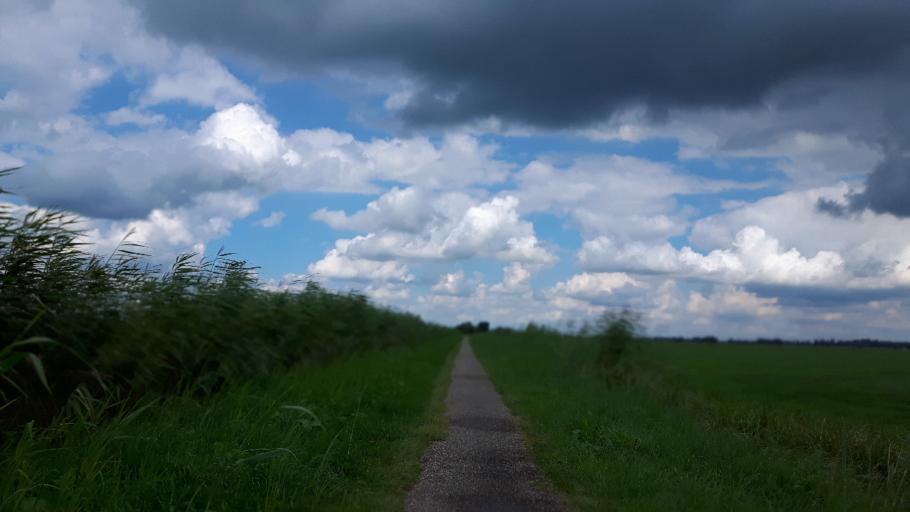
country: NL
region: Utrecht
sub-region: Gemeente Woerden
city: Woerden
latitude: 52.1285
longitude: 4.9430
